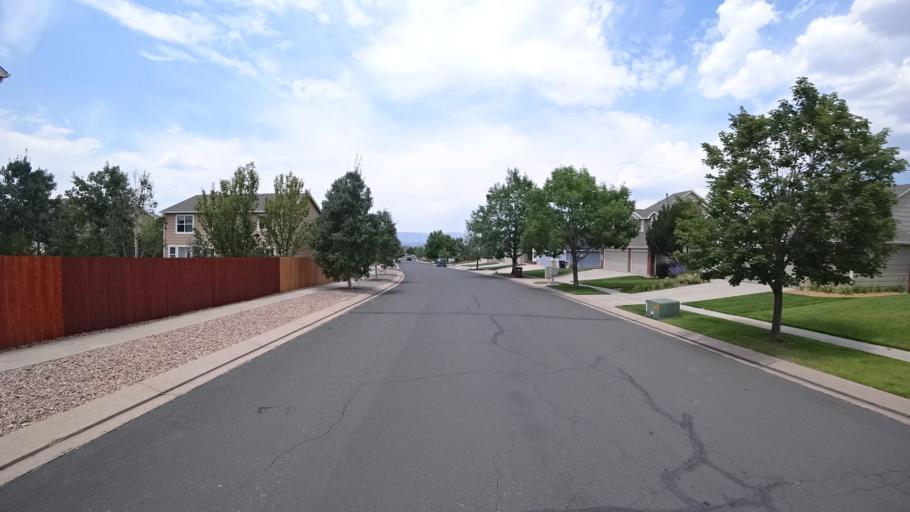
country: US
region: Colorado
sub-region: El Paso County
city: Black Forest
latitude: 38.9646
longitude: -104.7703
